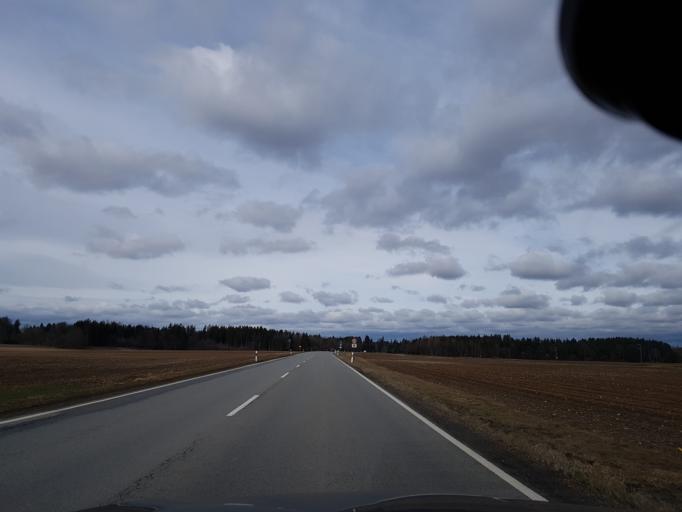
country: DE
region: Bavaria
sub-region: Upper Bavaria
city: Aying
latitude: 47.9743
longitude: 11.7608
